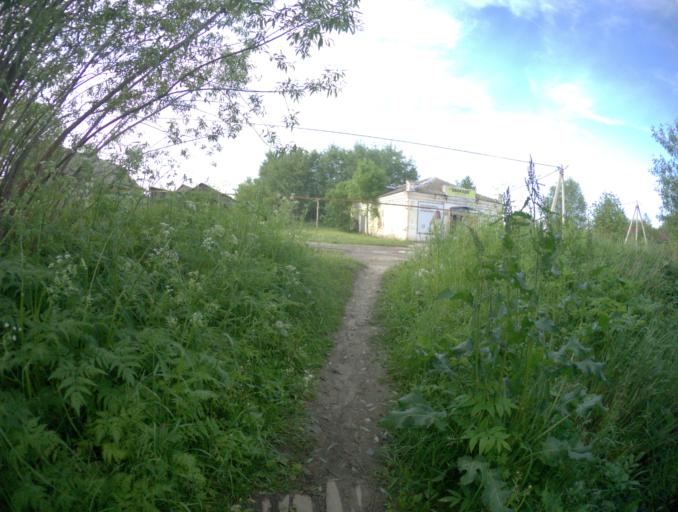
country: RU
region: Vladimir
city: Zolotkovo
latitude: 55.5049
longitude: 40.9619
